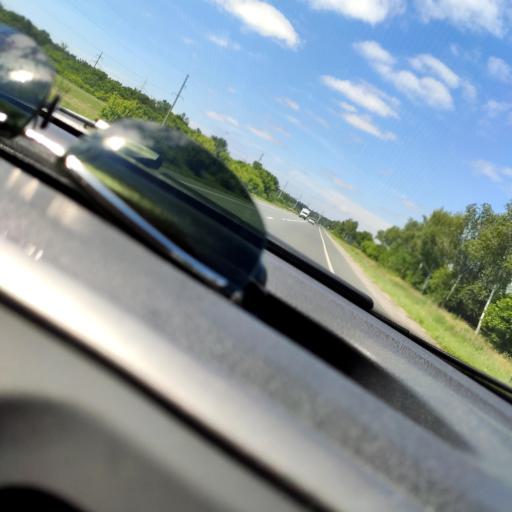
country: RU
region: Samara
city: Kurumoch
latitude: 53.4895
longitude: 49.9884
